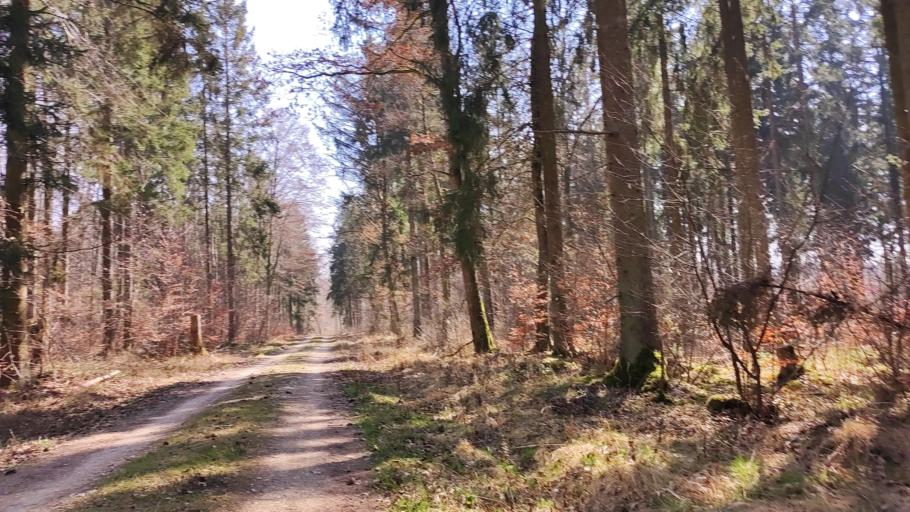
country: DE
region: Baden-Wuerttemberg
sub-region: Tuebingen Region
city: Borslingen
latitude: 48.5215
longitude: 10.0443
